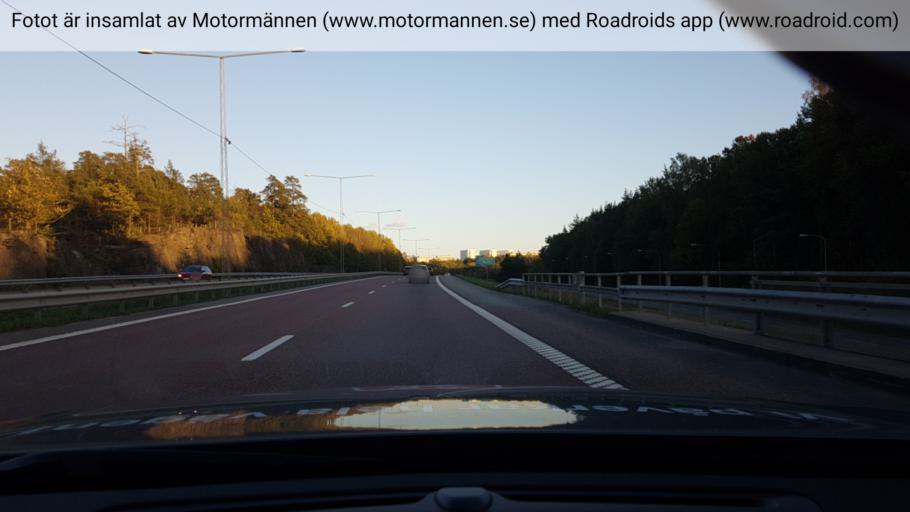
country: SE
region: Stockholm
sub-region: Nacka Kommun
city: Alta
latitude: 59.2606
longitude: 18.1593
